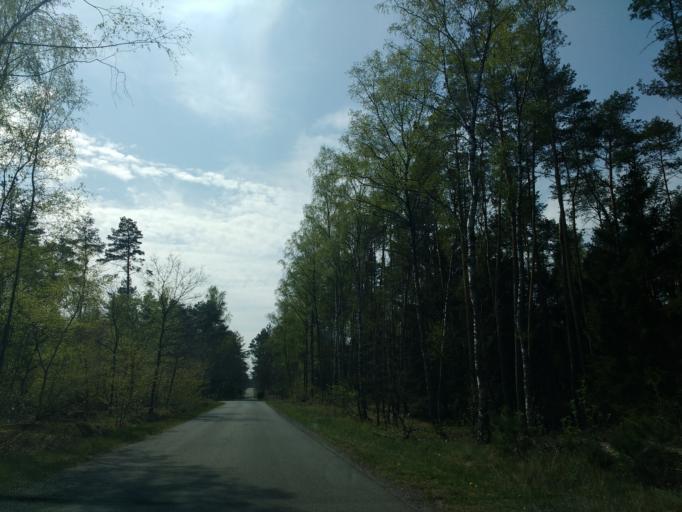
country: DE
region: North Rhine-Westphalia
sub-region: Regierungsbezirk Detmold
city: Hovelhof
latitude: 51.8469
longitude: 8.6825
